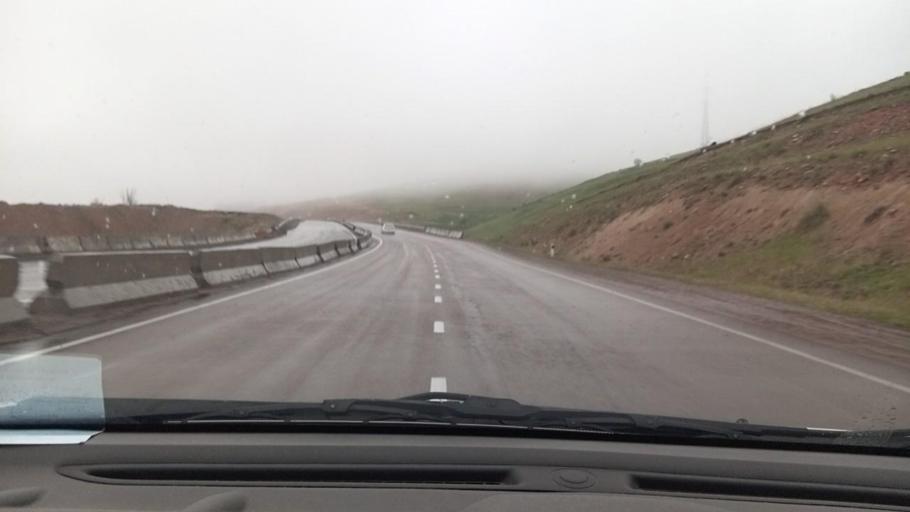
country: UZ
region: Toshkent
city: Angren
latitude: 41.0602
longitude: 70.1861
